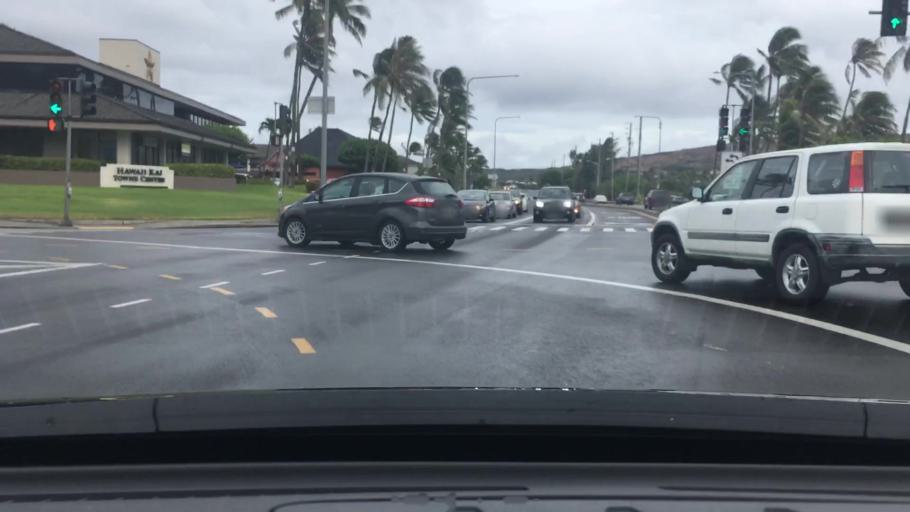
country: US
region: Hawaii
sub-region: Honolulu County
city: Waimanalo Beach
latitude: 21.2832
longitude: -157.7154
